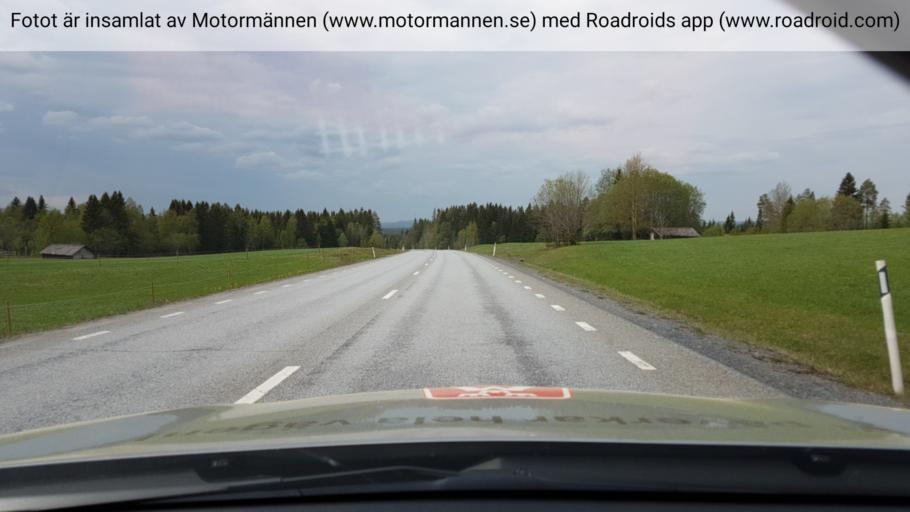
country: SE
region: Jaemtland
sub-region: Krokoms Kommun
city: Valla
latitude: 63.3059
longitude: 13.8705
